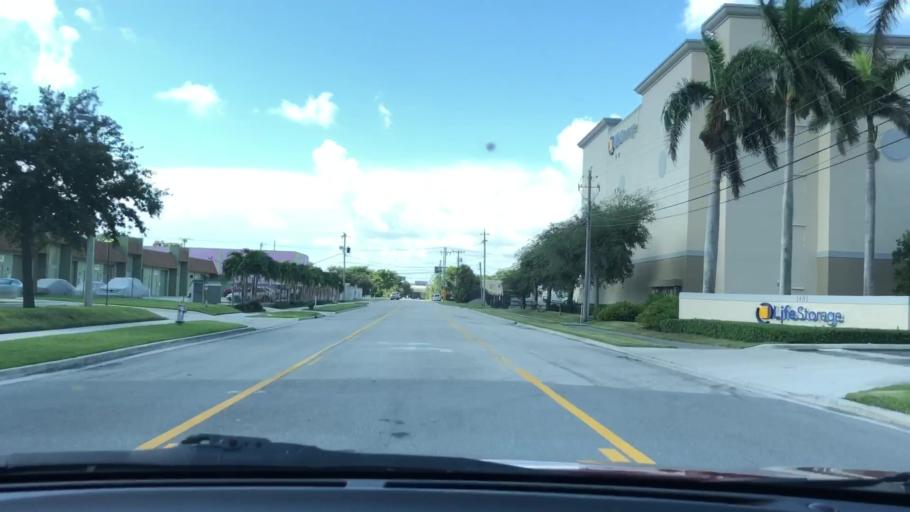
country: US
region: Florida
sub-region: Palm Beach County
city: West Palm Beach
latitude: 26.7013
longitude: -80.0676
